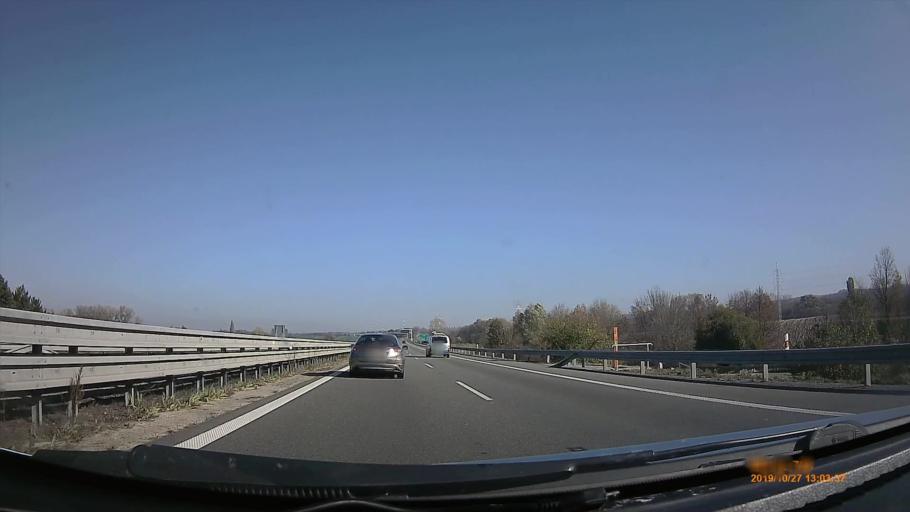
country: CZ
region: South Moravian
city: Drnovice
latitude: 49.2544
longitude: 16.9750
